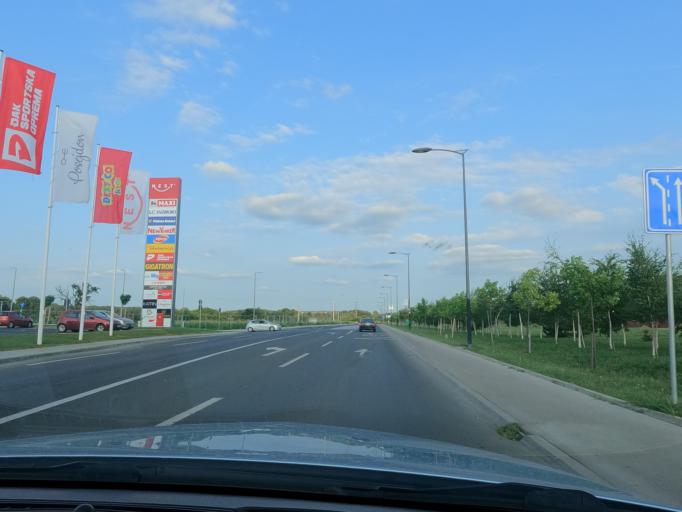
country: RS
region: Central Serbia
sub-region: Belgrade
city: Obrenovac
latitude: 44.6578
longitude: 20.2134
